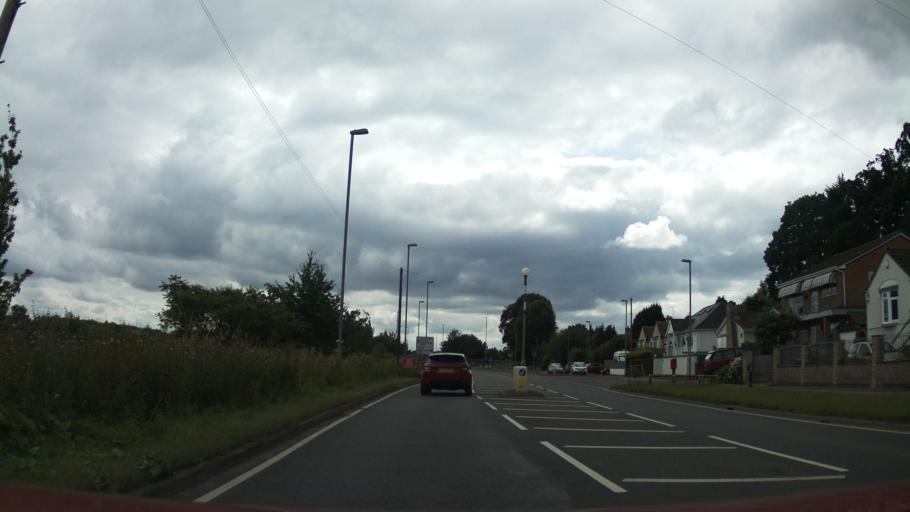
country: GB
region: England
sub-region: Nottinghamshire
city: Burton Joyce
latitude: 52.9785
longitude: -1.0578
